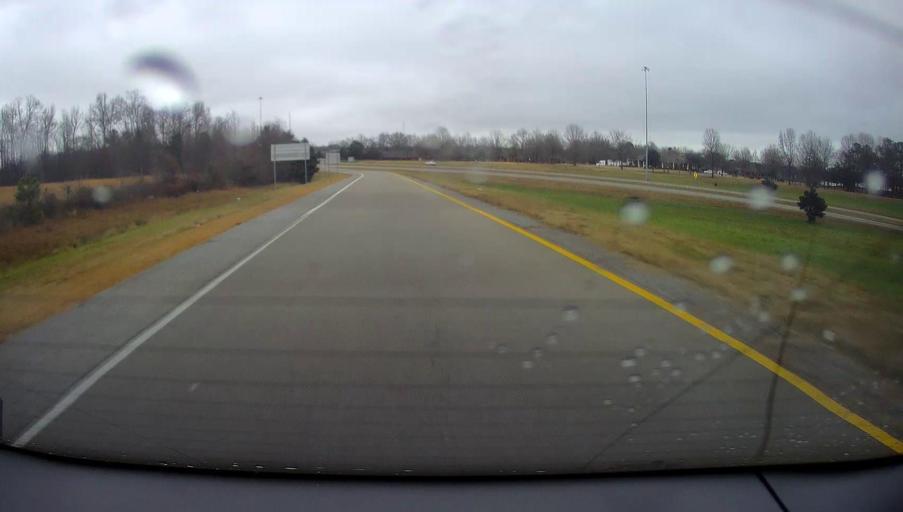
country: US
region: Mississippi
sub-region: Alcorn County
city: Corinth
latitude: 34.9097
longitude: -88.5454
